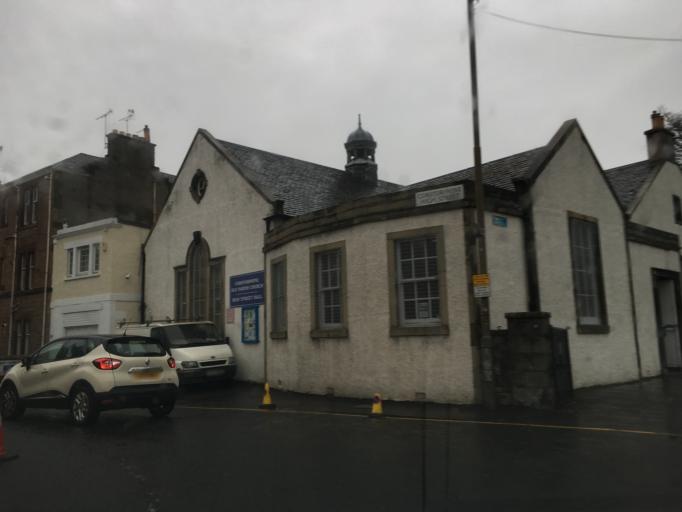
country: GB
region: Scotland
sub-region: Edinburgh
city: Colinton
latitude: 55.9408
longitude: -3.2821
